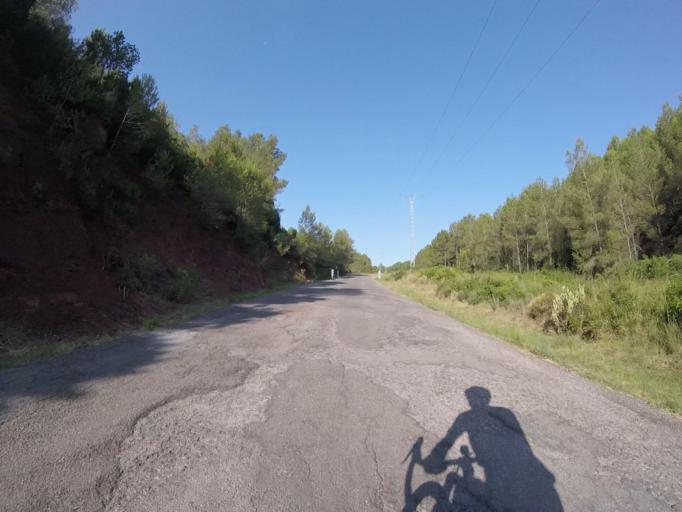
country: ES
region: Valencia
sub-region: Provincia de Castello
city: Benicassim
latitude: 40.0788
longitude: 0.0512
